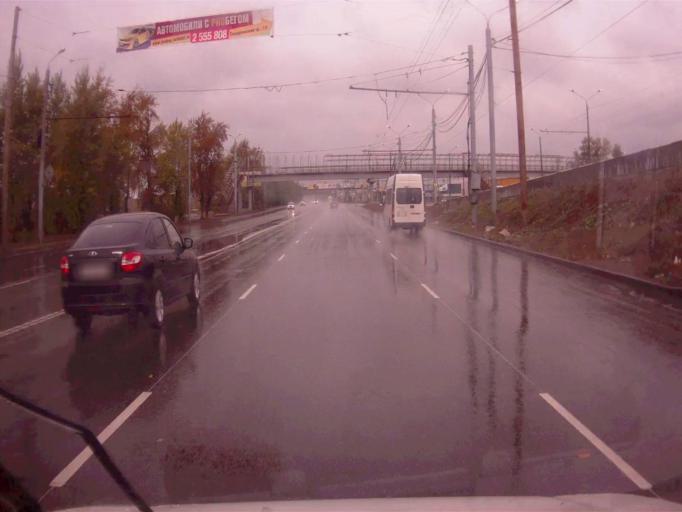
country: RU
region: Chelyabinsk
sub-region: Gorod Chelyabinsk
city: Chelyabinsk
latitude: 55.1998
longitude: 61.3859
